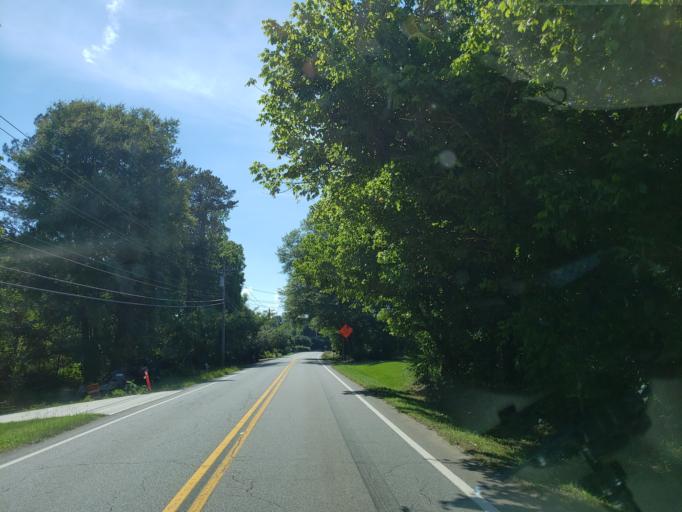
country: US
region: Georgia
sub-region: Cherokee County
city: Woodstock
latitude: 34.1110
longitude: -84.4535
